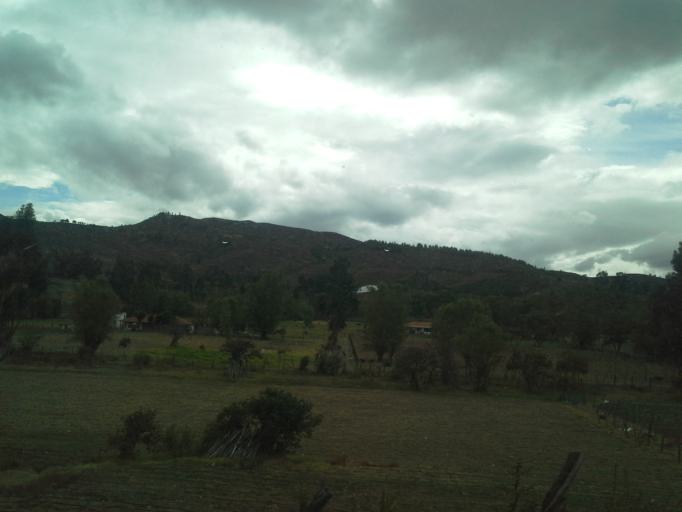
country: CO
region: Boyaca
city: Raquira
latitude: 5.5618
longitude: -73.6459
